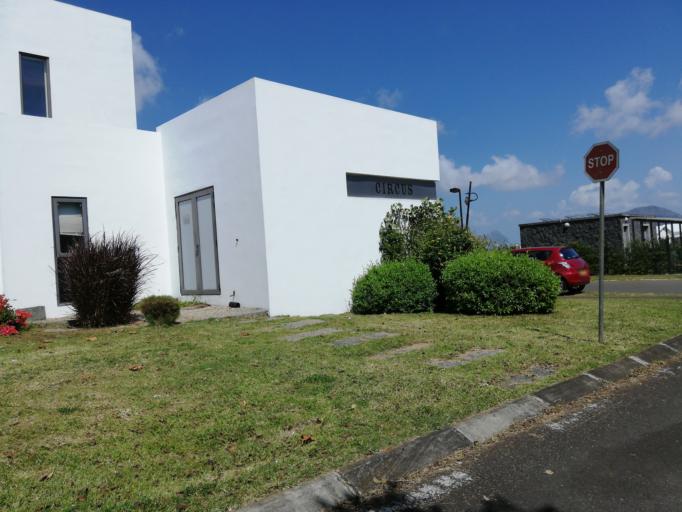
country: MU
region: Moka
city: Saint Pierre
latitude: -20.2276
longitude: 57.5111
